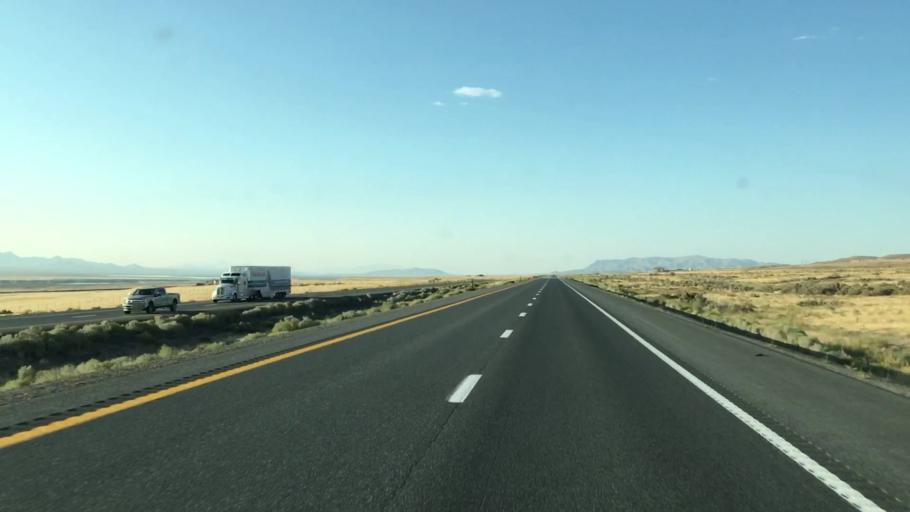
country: US
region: Nevada
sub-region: Pershing County
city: Lovelock
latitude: 40.4968
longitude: -118.2834
